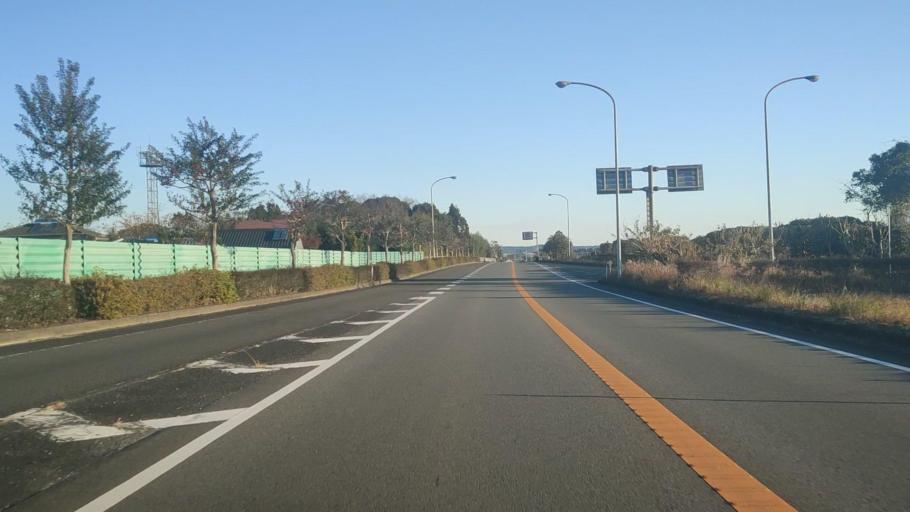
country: JP
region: Miyazaki
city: Tsuma
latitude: 32.0373
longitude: 131.4668
